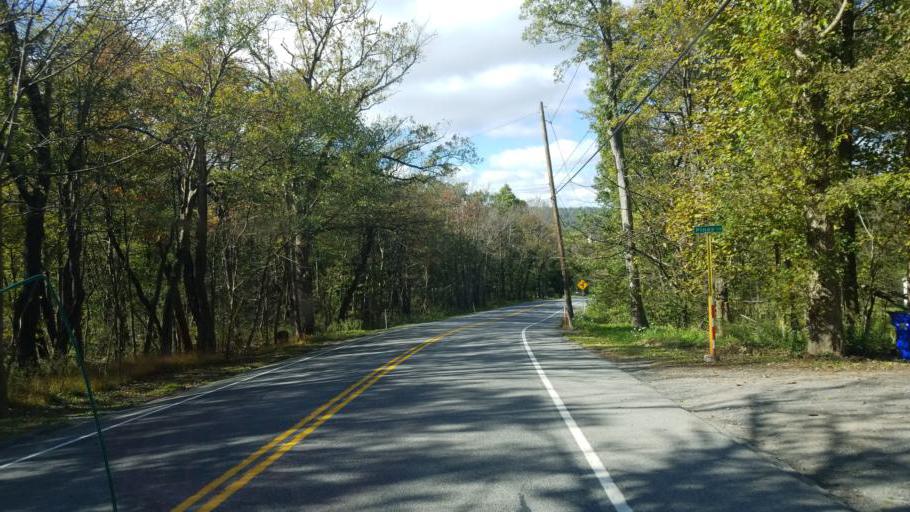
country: US
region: Pennsylvania
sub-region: Bedford County
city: Earlston
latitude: 40.0203
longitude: -78.1796
